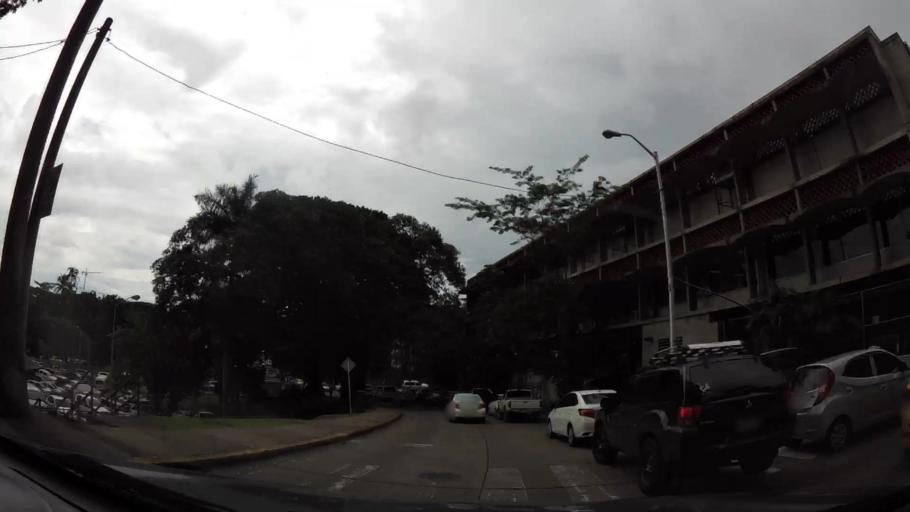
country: PA
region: Panama
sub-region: Distrito de Panama
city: Ancon
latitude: 8.9604
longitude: -79.5455
